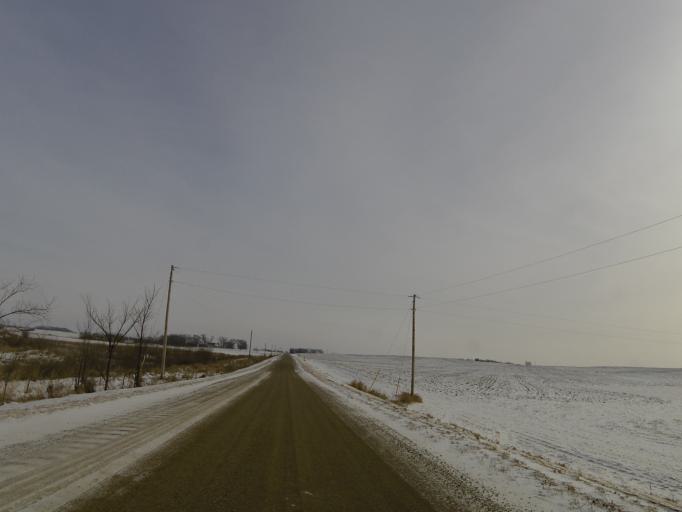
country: US
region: Minnesota
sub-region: Carver County
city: Mayer
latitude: 44.8912
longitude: -93.8727
